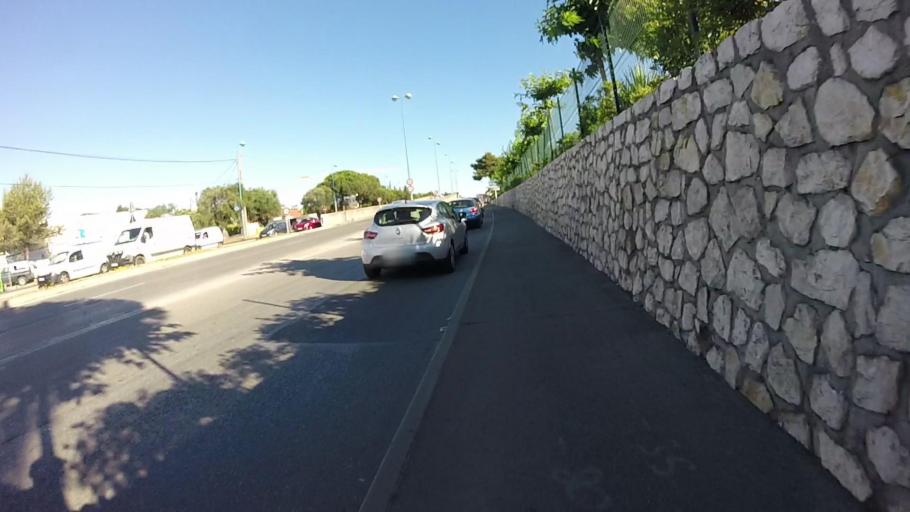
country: FR
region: Provence-Alpes-Cote d'Azur
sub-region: Departement des Alpes-Maritimes
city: Biot
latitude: 43.6001
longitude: 7.0859
